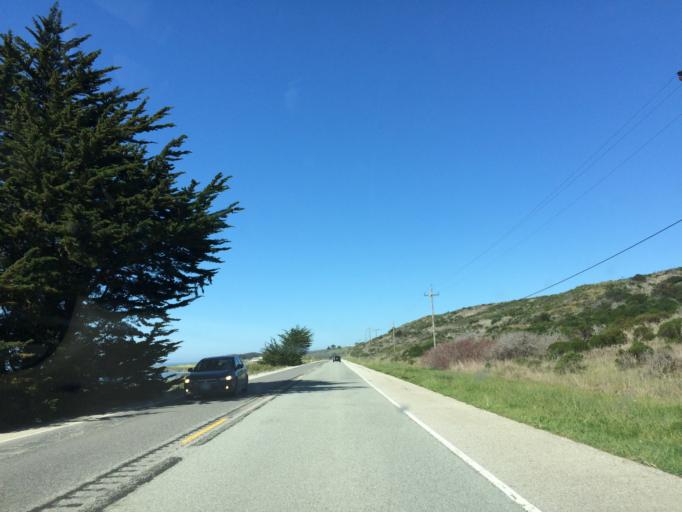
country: US
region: California
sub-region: San Mateo County
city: Portola Valley
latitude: 37.1781
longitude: -122.3709
